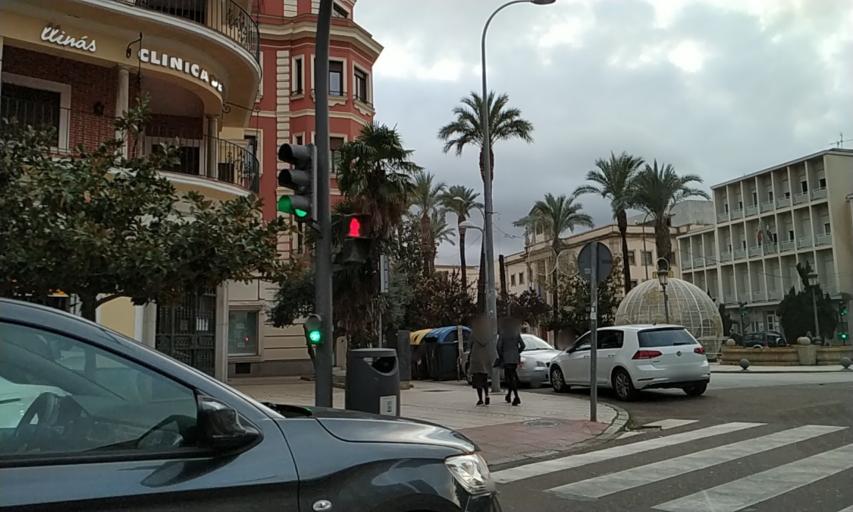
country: ES
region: Extremadura
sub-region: Provincia de Badajoz
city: Badajoz
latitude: 38.8753
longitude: -6.9737
